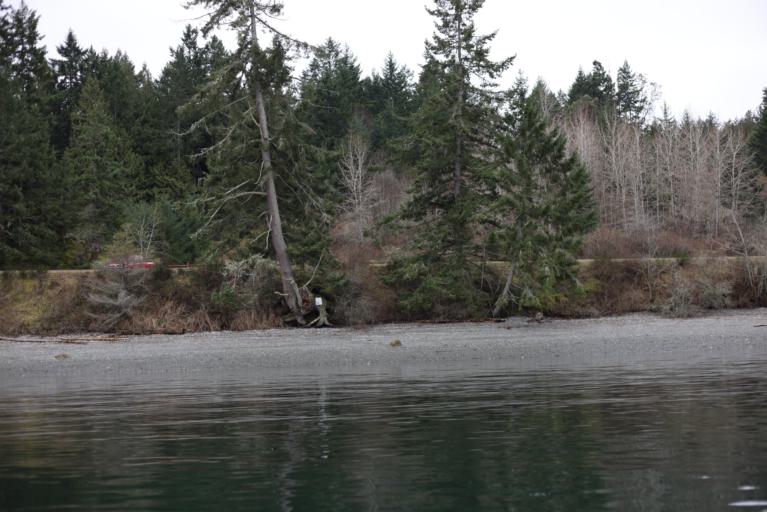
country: CA
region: British Columbia
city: North Saanich
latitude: 48.6334
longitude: -123.5309
